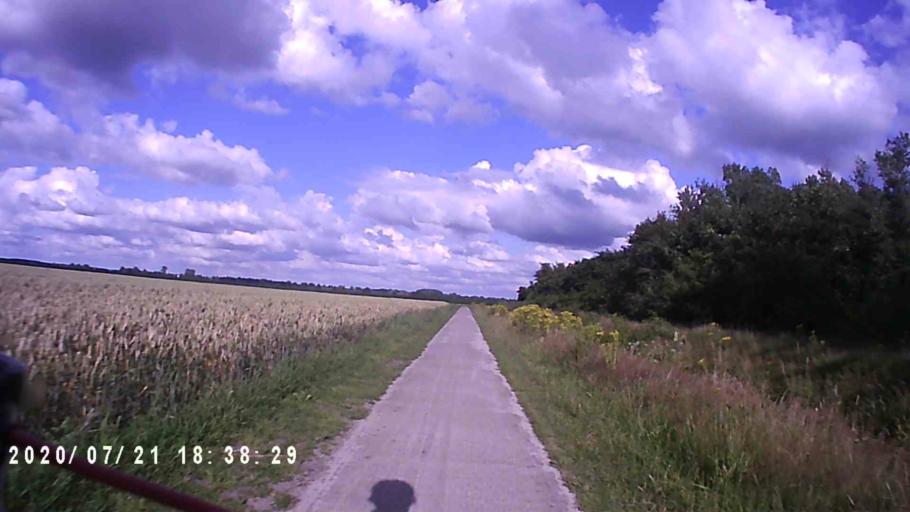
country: NL
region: Groningen
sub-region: Gemeente Hoogezand-Sappemeer
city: Hoogezand
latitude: 53.1951
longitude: 6.7456
